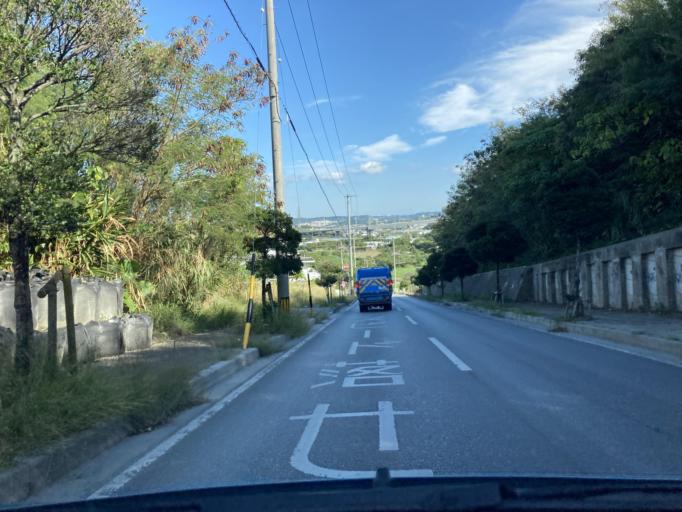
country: JP
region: Okinawa
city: Tomigusuku
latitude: 26.1697
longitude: 127.6999
